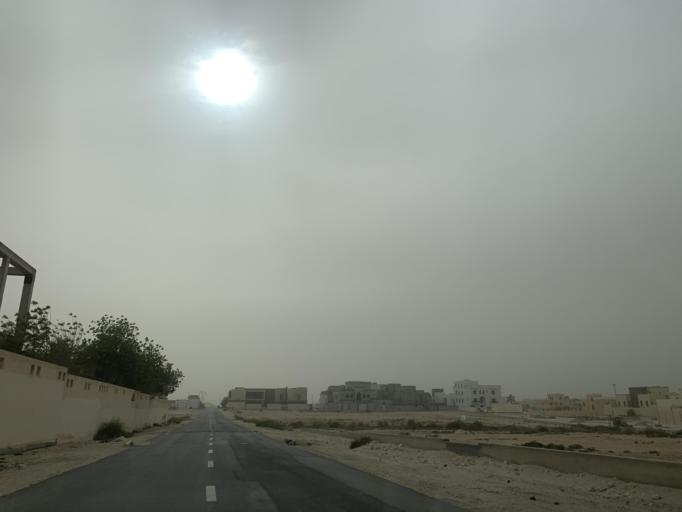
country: BH
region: Northern
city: Ar Rifa'
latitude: 26.1441
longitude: 50.5306
